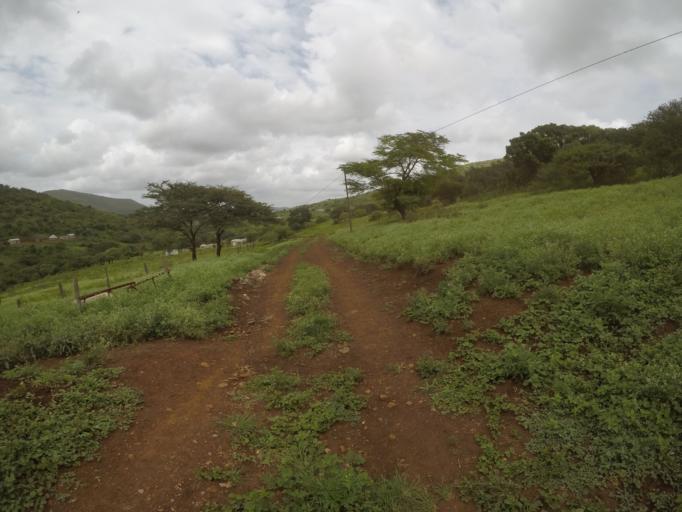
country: ZA
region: KwaZulu-Natal
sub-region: uThungulu District Municipality
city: Empangeni
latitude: -28.5801
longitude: 31.8892
